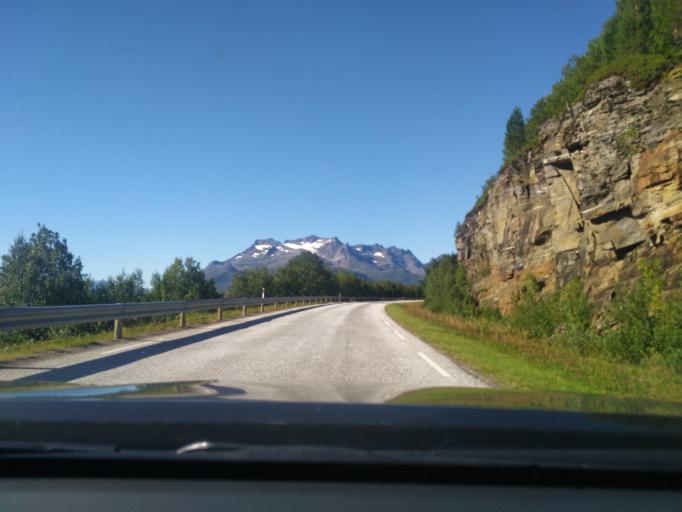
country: NO
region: Troms
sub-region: Dyroy
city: Brostadbotn
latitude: 68.9178
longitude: 17.5971
